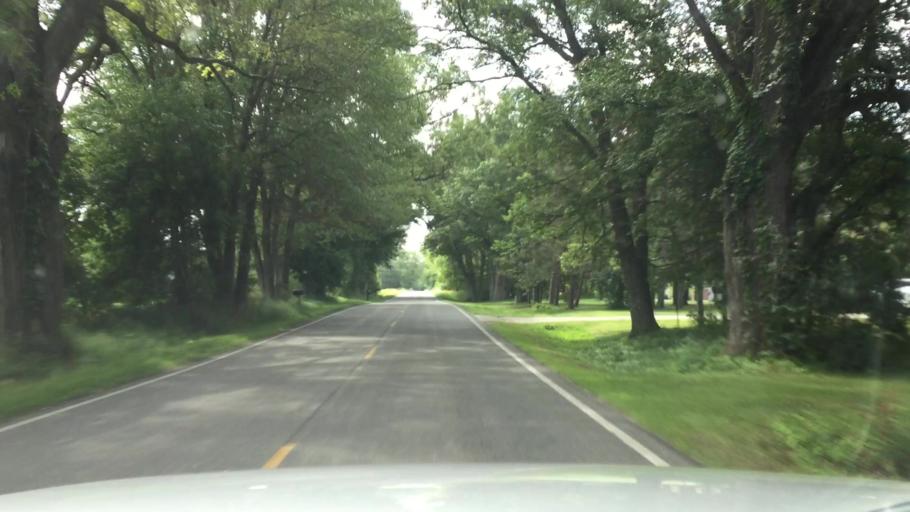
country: US
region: Michigan
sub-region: Montcalm County
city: Greenville
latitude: 43.1647
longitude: -85.2135
